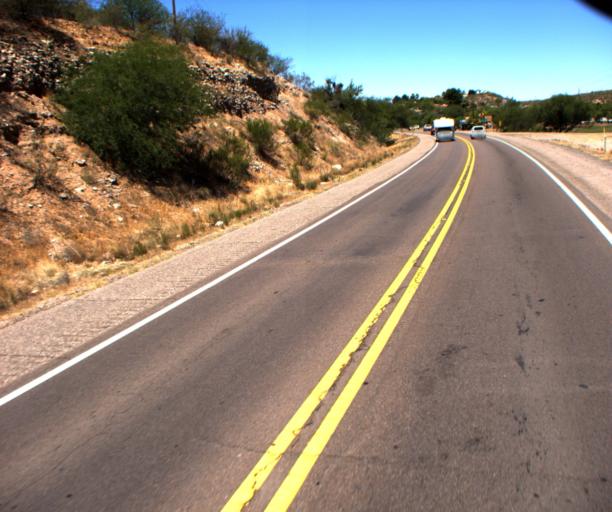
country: US
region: Arizona
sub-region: Maricopa County
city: Wickenburg
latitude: 33.9891
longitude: -112.7430
